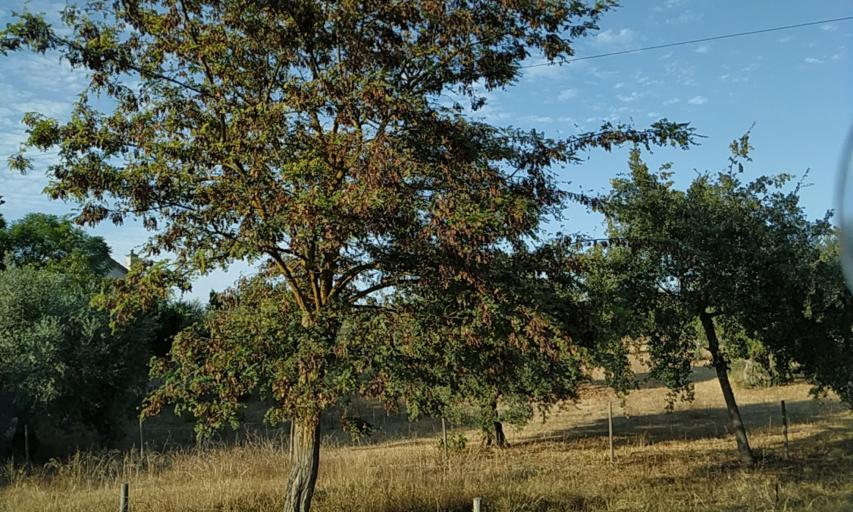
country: PT
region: Santarem
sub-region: Santarem
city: Santarem
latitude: 39.3345
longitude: -8.6610
